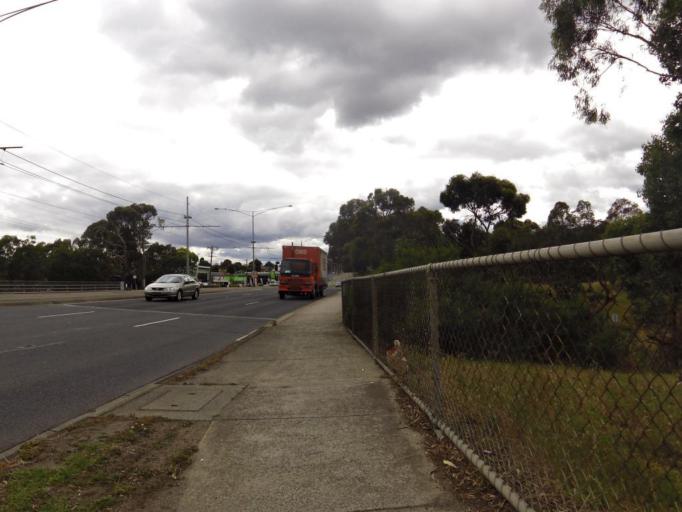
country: AU
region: Victoria
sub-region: Darebin
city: Kingsbury
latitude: -37.7211
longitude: 145.0343
